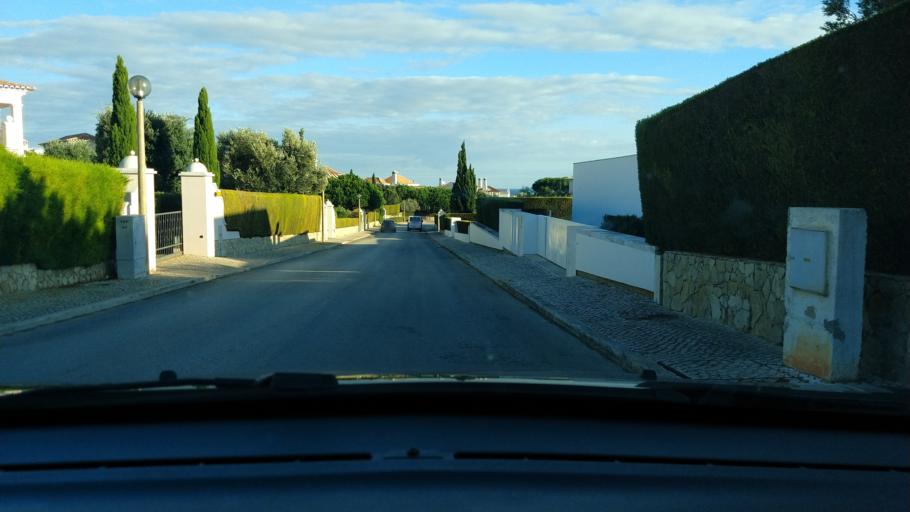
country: PT
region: Faro
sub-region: Vila do Bispo
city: Sagres
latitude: 37.0238
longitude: -8.9291
